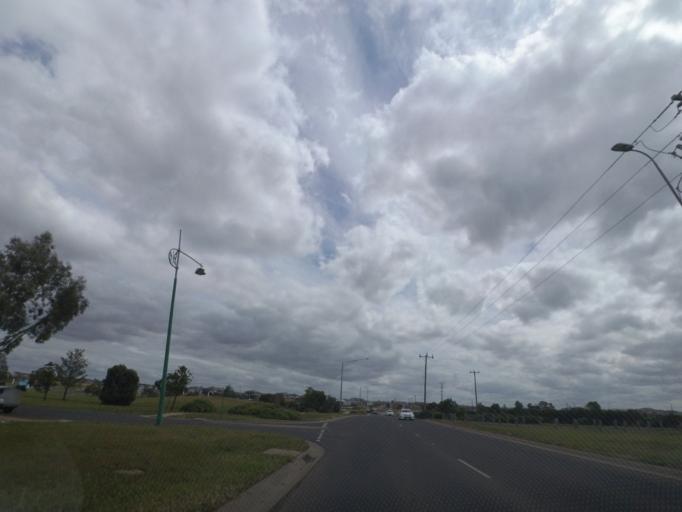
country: AU
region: Victoria
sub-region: Wyndham
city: Tarneit
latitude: -37.8450
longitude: 144.6537
